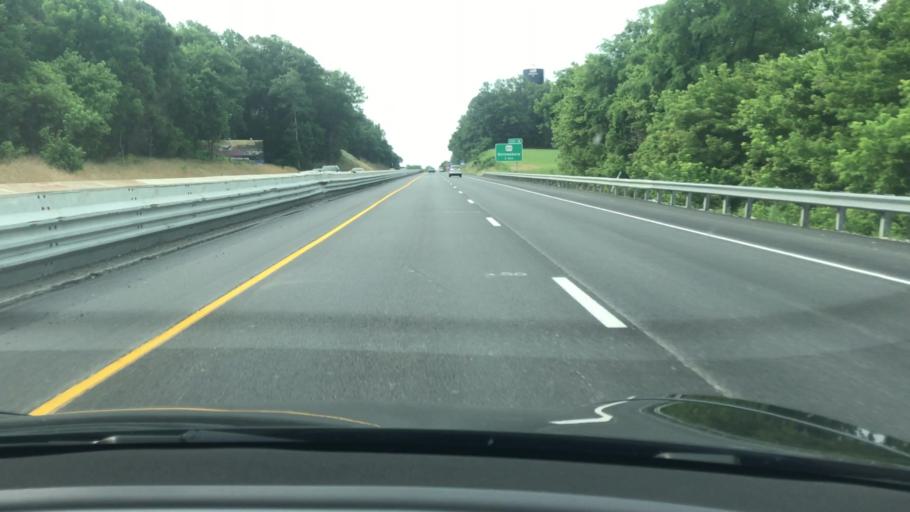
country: US
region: Pennsylvania
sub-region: York County
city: Shrewsbury
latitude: 39.7908
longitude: -76.6751
